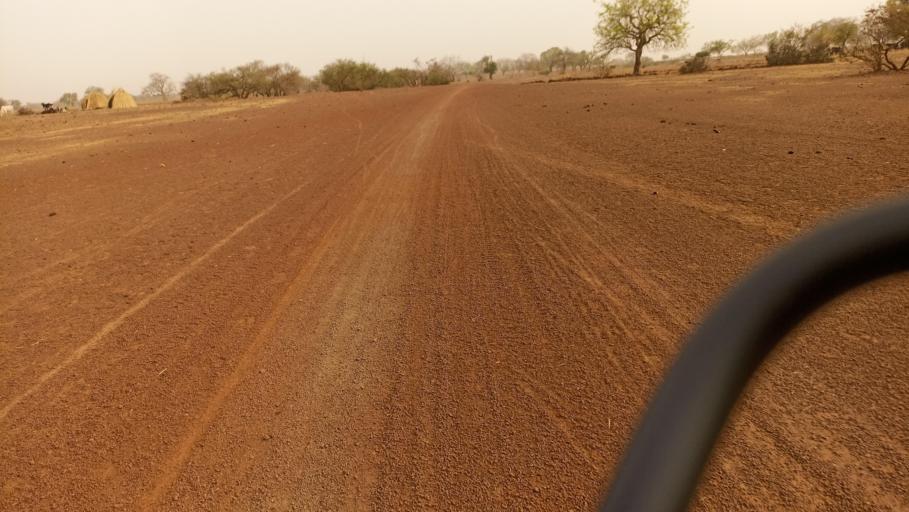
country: BF
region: Nord
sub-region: Province du Zondoma
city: Gourcy
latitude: 13.1453
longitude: -2.5975
